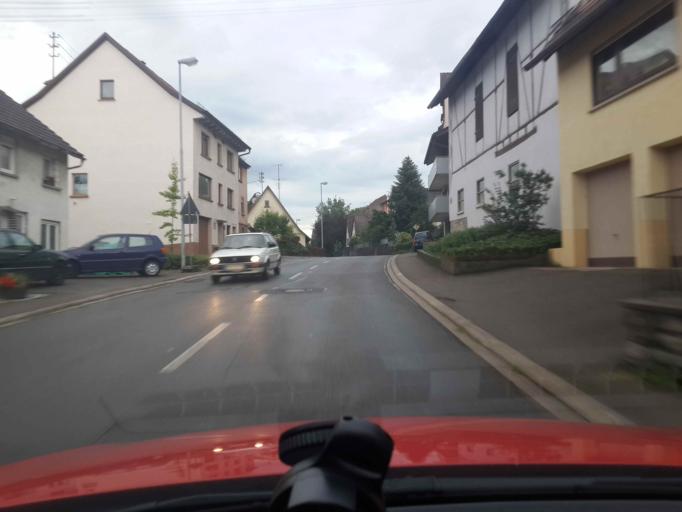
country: DE
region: Baden-Wuerttemberg
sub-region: Karlsruhe Region
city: Billigheim
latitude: 49.3482
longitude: 9.2222
